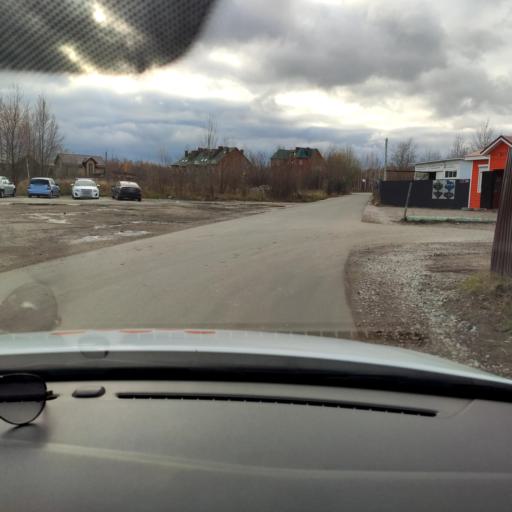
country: RU
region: Tatarstan
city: Stolbishchi
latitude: 55.7380
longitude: 49.2688
